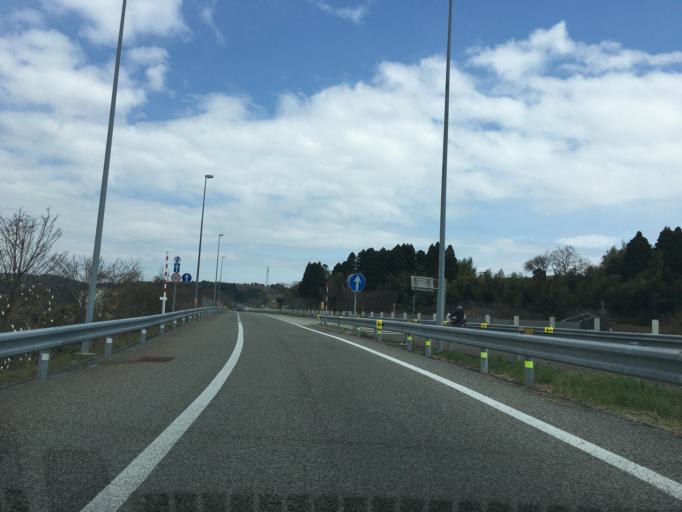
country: JP
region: Toyama
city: Kuragaki-kosugi
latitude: 36.6814
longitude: 137.1347
